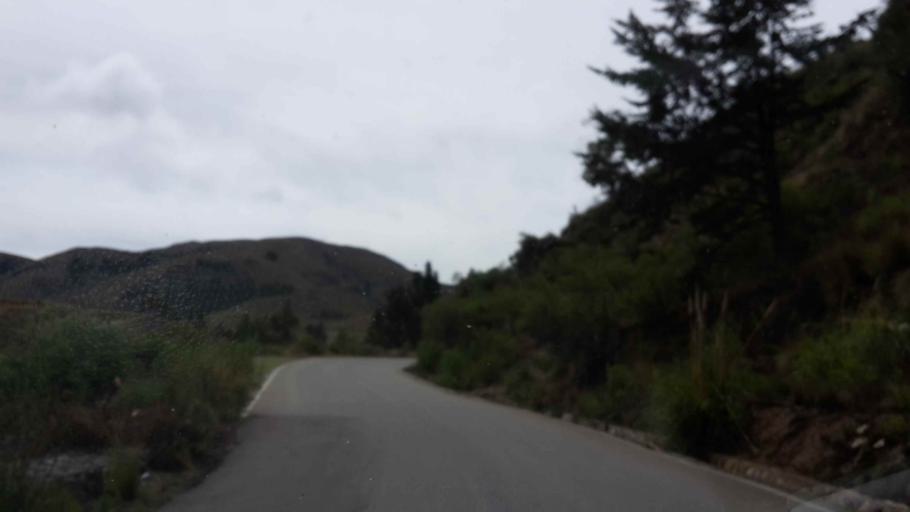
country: BO
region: Cochabamba
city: Colomi
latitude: -17.4017
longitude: -65.8103
